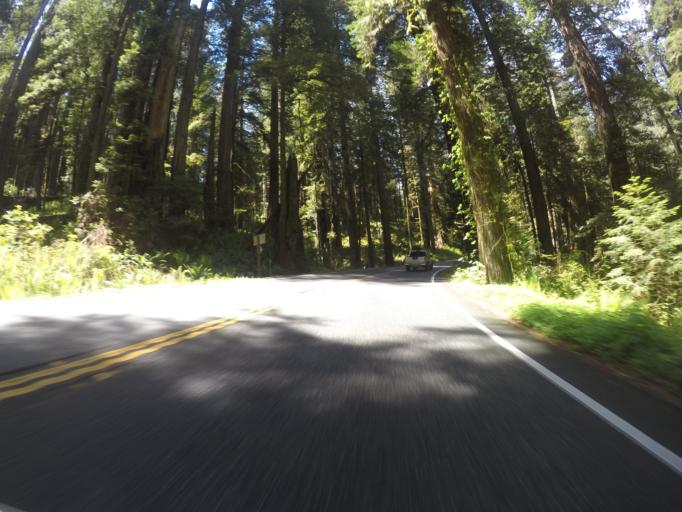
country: US
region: California
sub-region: Del Norte County
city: Bertsch-Oceanview
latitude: 41.8104
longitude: -124.1184
